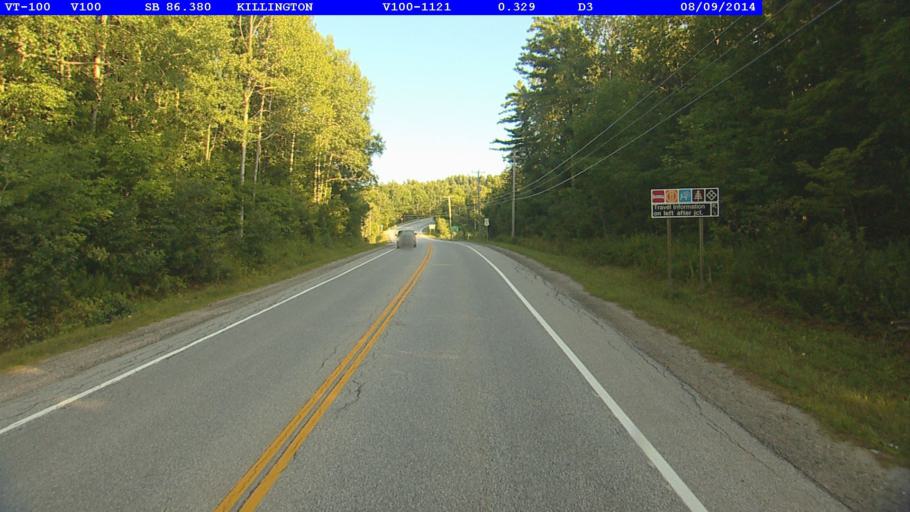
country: US
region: Vermont
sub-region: Rutland County
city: Rutland
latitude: 43.6720
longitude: -72.8074
